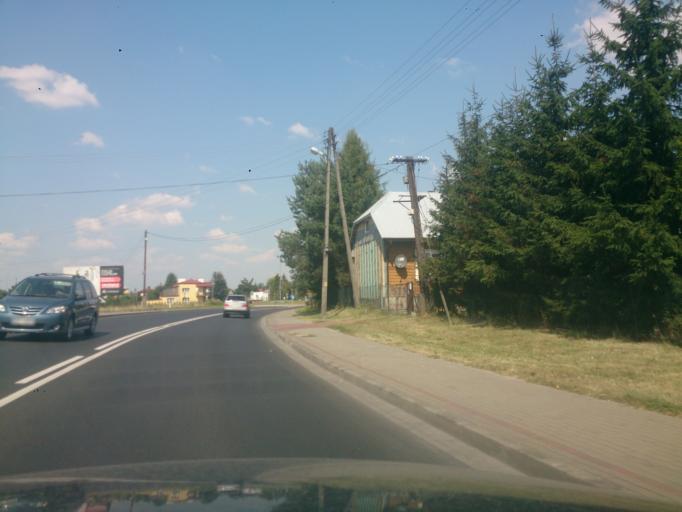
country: PL
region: Subcarpathian Voivodeship
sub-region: Powiat kolbuszowski
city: Kolbuszowa
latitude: 50.2497
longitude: 21.7740
